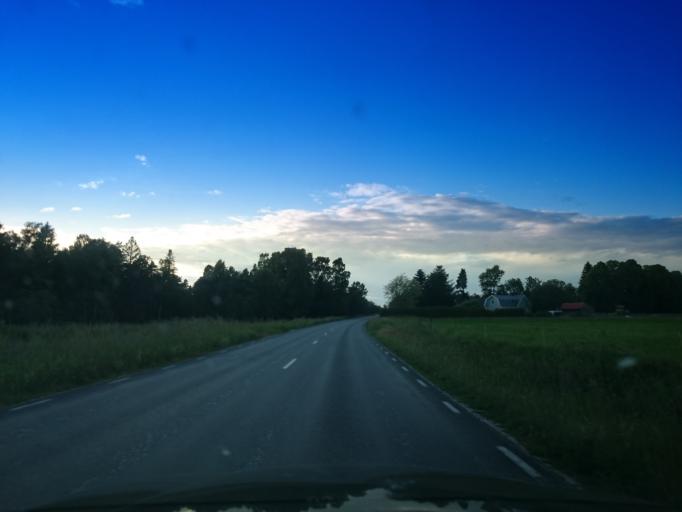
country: SE
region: Gotland
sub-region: Gotland
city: Hemse
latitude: 57.3271
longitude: 18.3812
